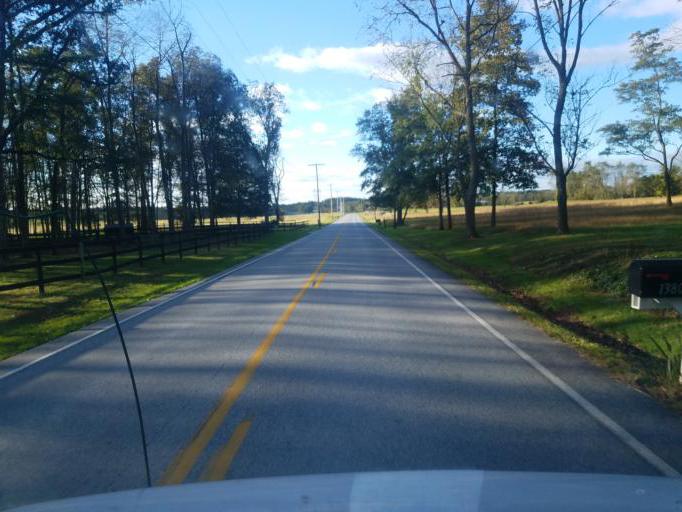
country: US
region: Pennsylvania
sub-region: Adams County
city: Biglerville
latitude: 39.8848
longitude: -77.2290
